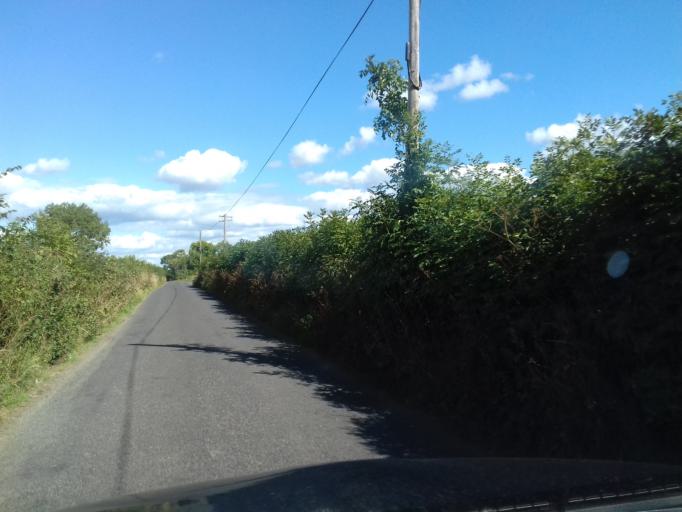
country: IE
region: Leinster
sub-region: Kilkenny
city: Callan
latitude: 52.5346
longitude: -7.3392
